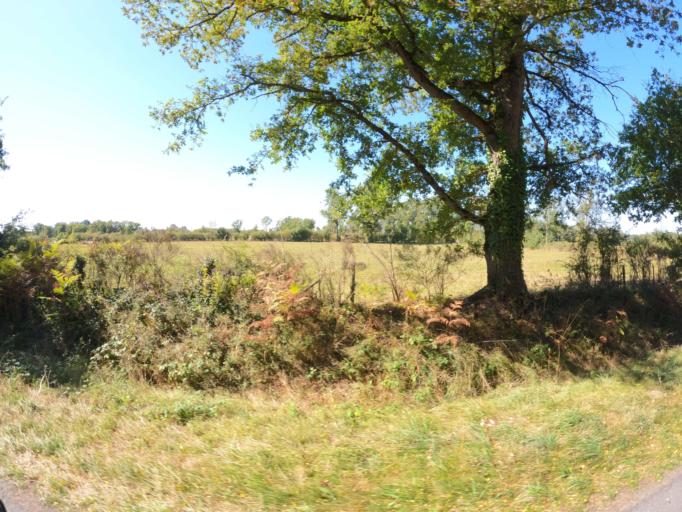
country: FR
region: Poitou-Charentes
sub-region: Departement de la Vienne
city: Lathus-Saint-Remy
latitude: 46.3112
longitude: 0.9801
